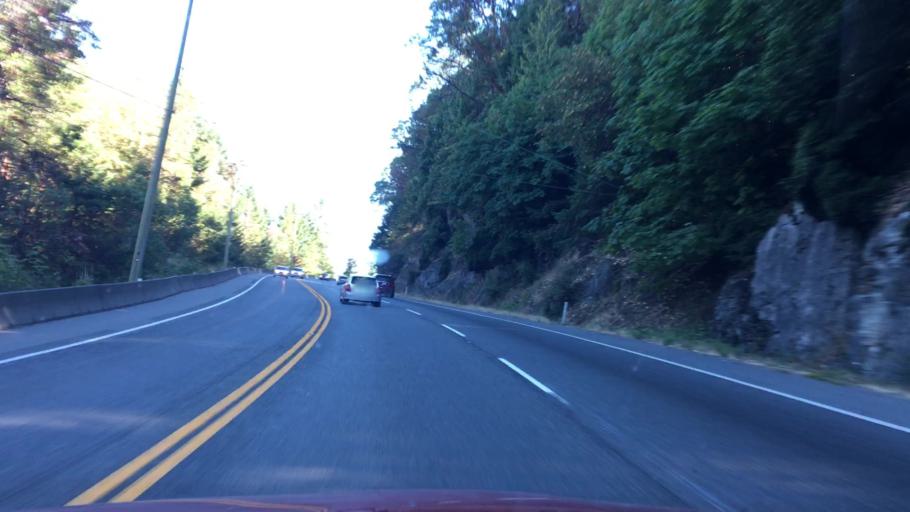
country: CA
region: British Columbia
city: North Saanich
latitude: 48.5938
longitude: -123.5336
